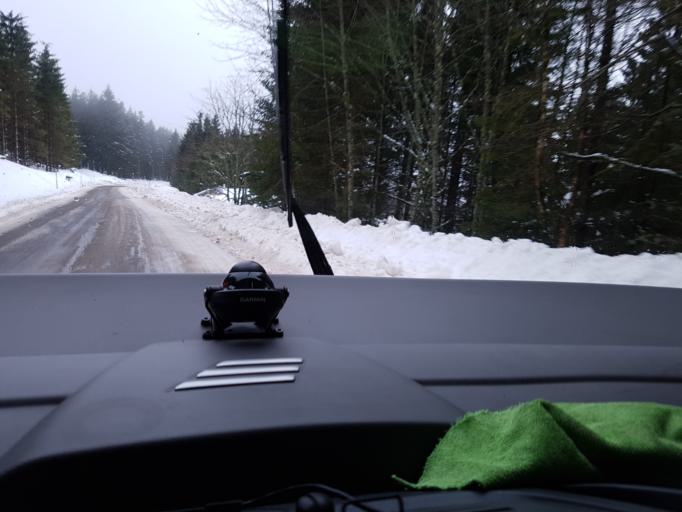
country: FR
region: Lorraine
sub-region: Departement des Vosges
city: Plainfaing
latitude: 48.1333
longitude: 7.0733
